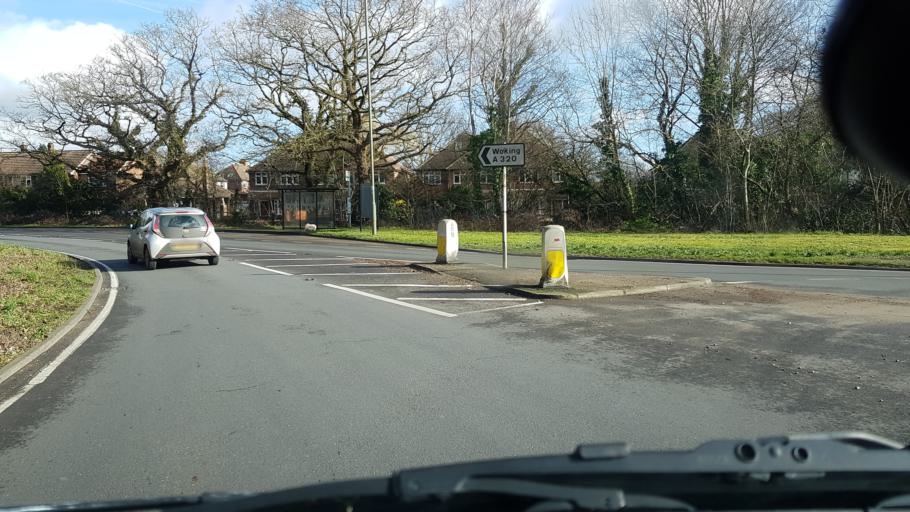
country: GB
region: England
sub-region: Surrey
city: Guildford
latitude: 51.2675
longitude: -0.5760
